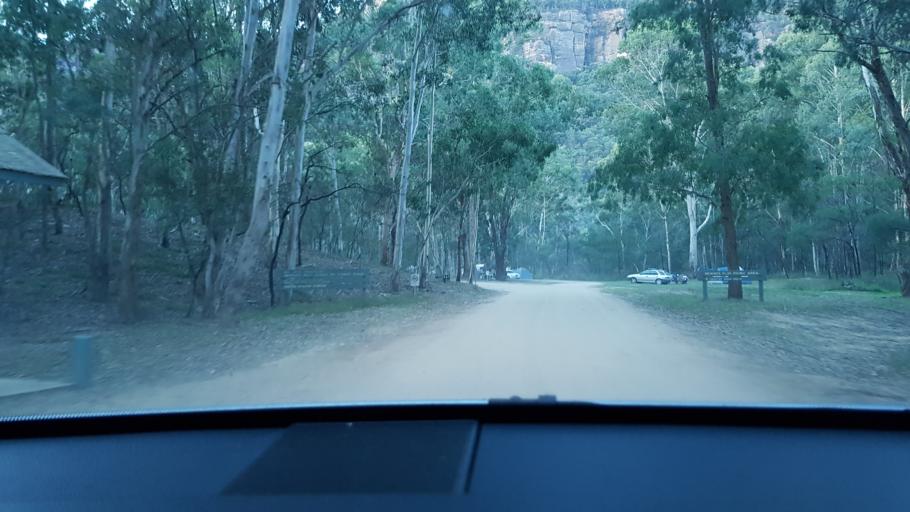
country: AU
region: New South Wales
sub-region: Lithgow
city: Portland
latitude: -33.1742
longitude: 150.2374
